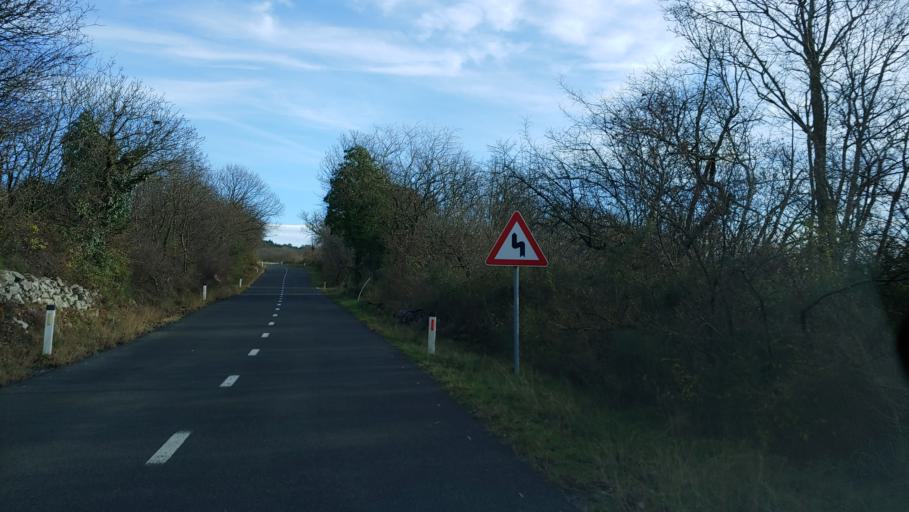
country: IT
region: Friuli Venezia Giulia
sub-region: Provincia di Trieste
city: Sistiana-Visogliano
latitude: 45.8098
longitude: 13.6857
